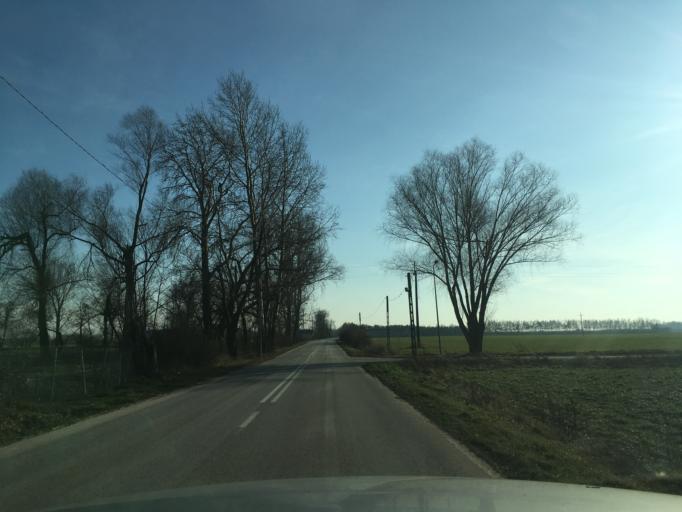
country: PL
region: Masovian Voivodeship
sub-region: Powiat pruszkowski
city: Nadarzyn
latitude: 52.0535
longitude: 20.8249
